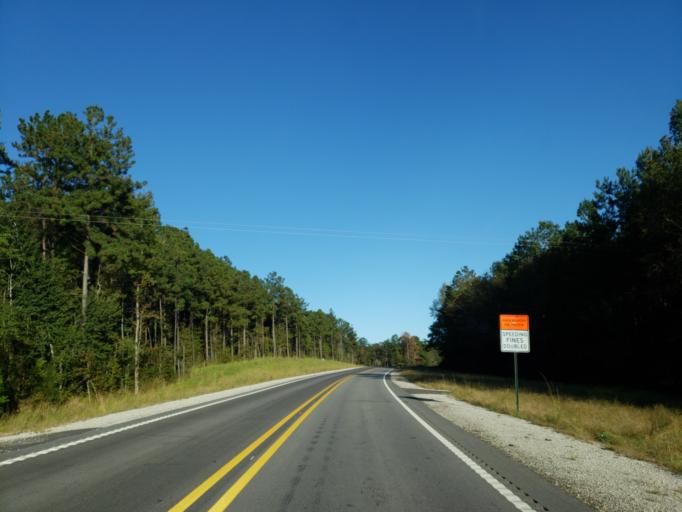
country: US
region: Mississippi
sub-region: Perry County
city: Richton
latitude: 31.3745
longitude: -88.8362
